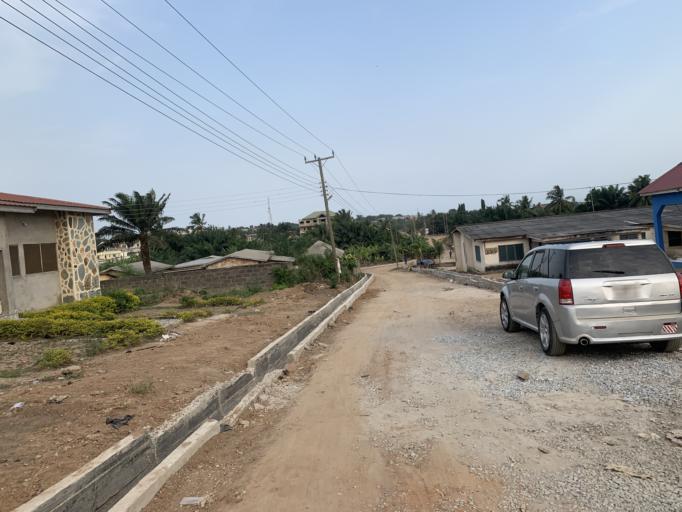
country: GH
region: Central
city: Winneba
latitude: 5.3569
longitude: -0.6266
